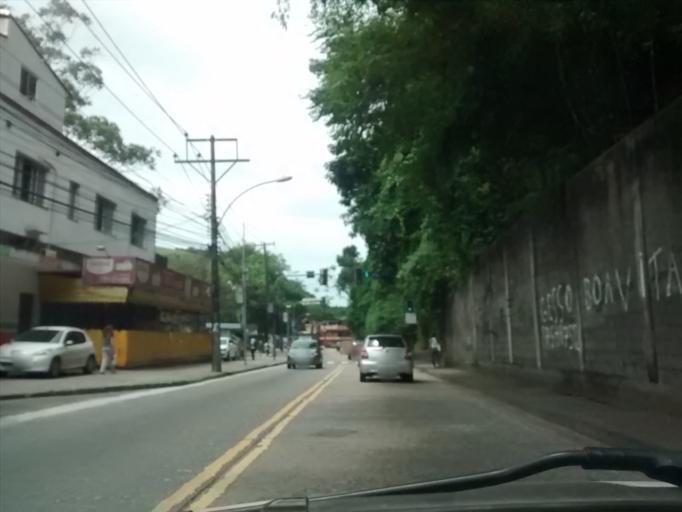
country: BR
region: Rio de Janeiro
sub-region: Rio De Janeiro
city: Rio de Janeiro
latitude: -22.9735
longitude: -43.2850
